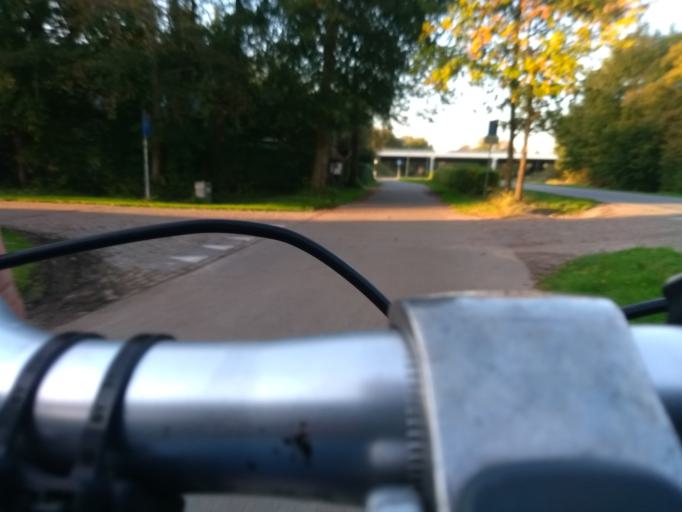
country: NL
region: Drenthe
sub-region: Gemeente Assen
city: Assen
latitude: 52.9686
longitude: 6.5546
